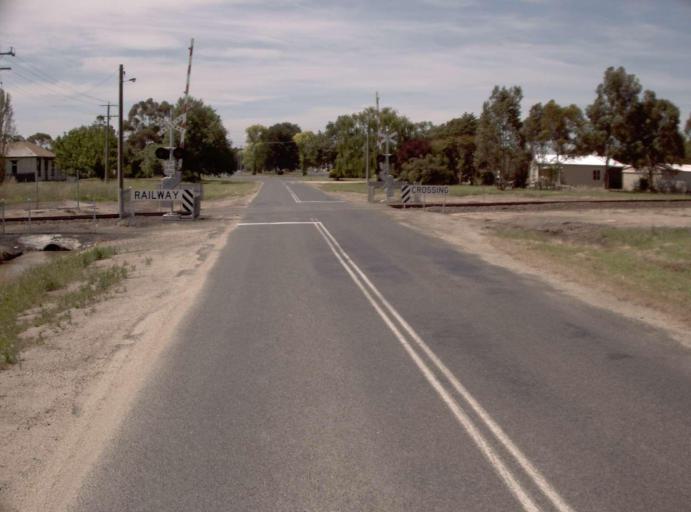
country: AU
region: Victoria
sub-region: Wellington
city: Heyfield
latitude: -38.1564
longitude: 146.7886
